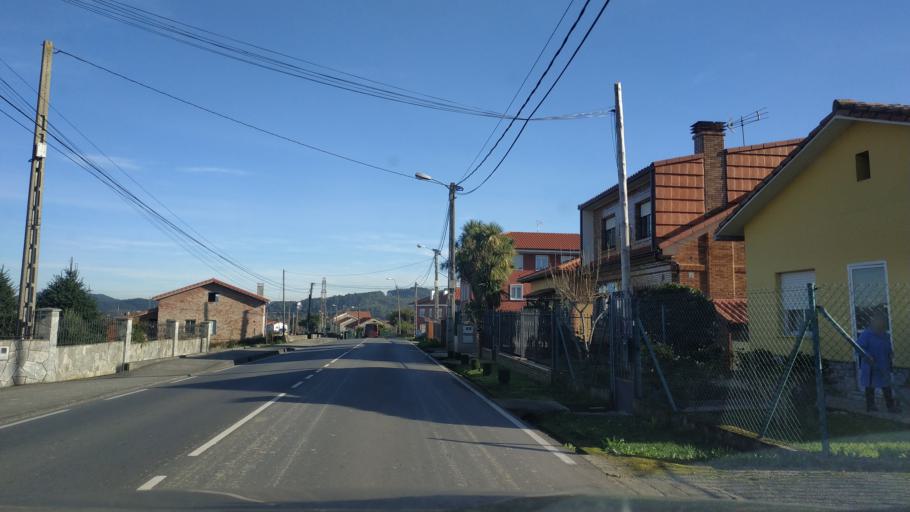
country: ES
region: Asturias
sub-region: Province of Asturias
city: Corvera de Asturias
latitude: 43.5387
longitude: -5.8850
